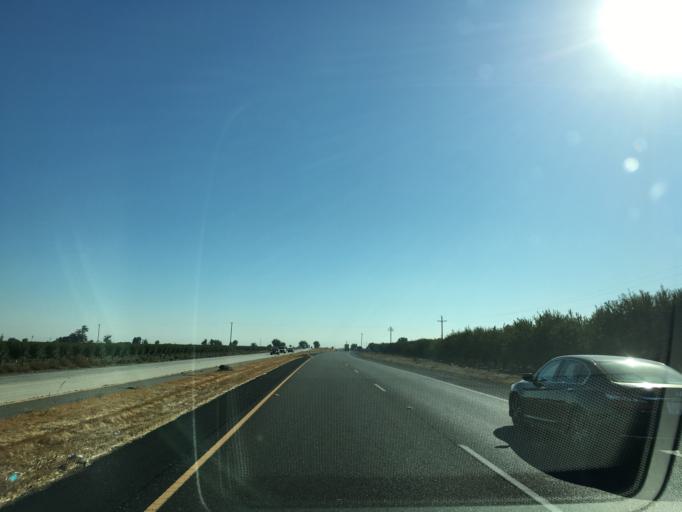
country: US
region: California
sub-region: Madera County
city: Chowchilla
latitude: 37.0833
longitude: -120.3686
